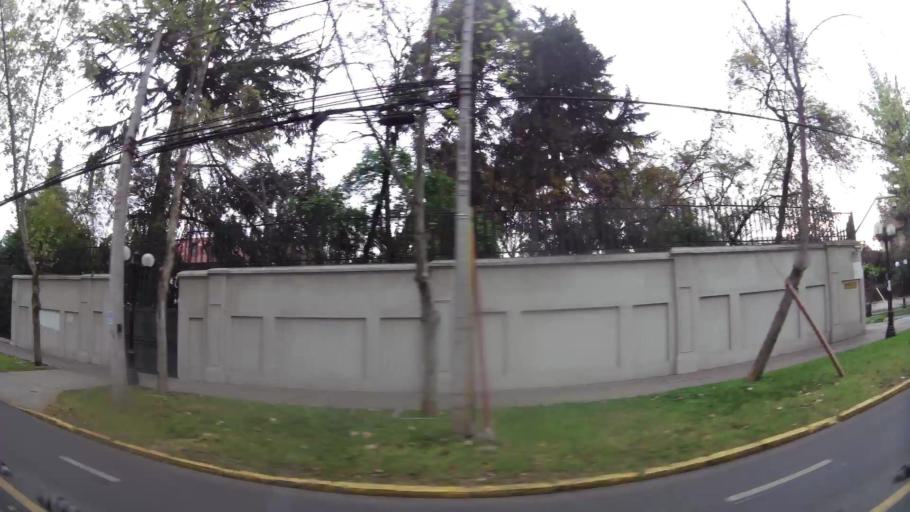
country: CL
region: Santiago Metropolitan
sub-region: Provincia de Santiago
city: Santiago
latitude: -33.4410
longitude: -70.6181
